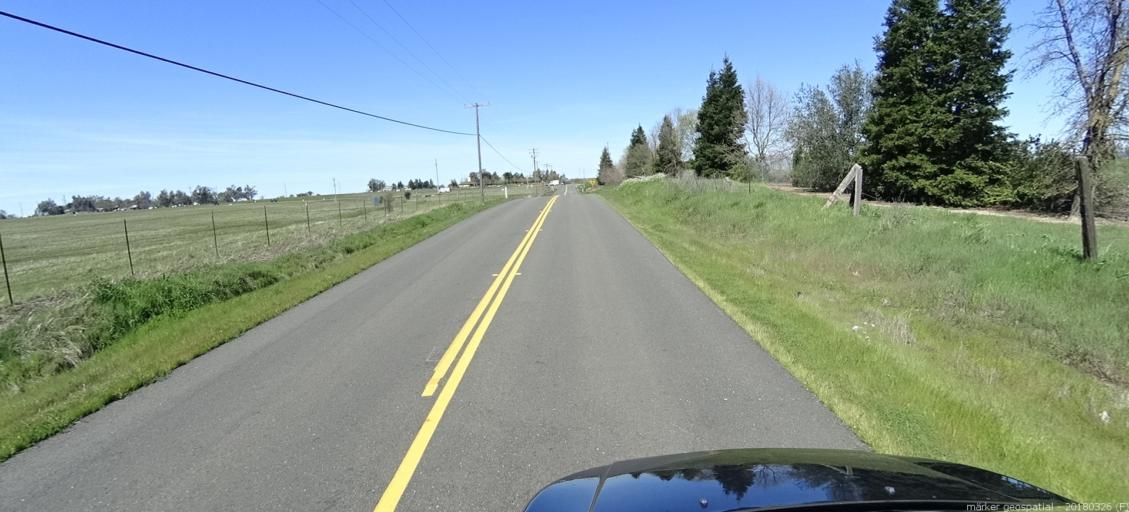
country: US
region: California
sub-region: Sacramento County
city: Rancho Cordova
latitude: 38.5070
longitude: -121.2610
